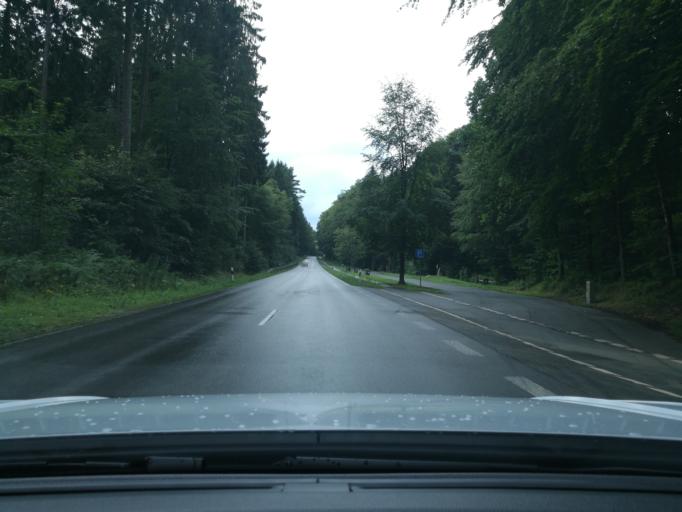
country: DE
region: Schleswig-Holstein
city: Dassendorf
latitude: 53.5171
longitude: 10.3520
